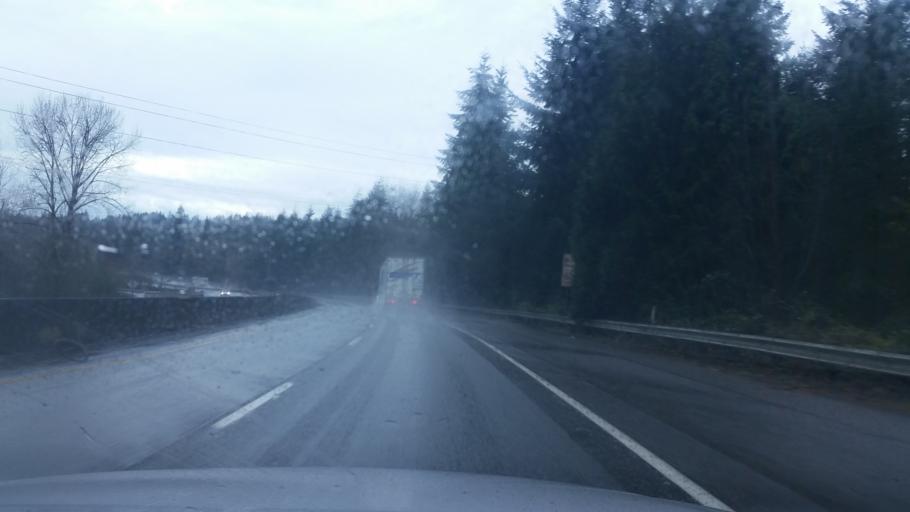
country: US
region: Washington
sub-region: King County
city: Hobart
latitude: 47.4359
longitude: -121.9736
